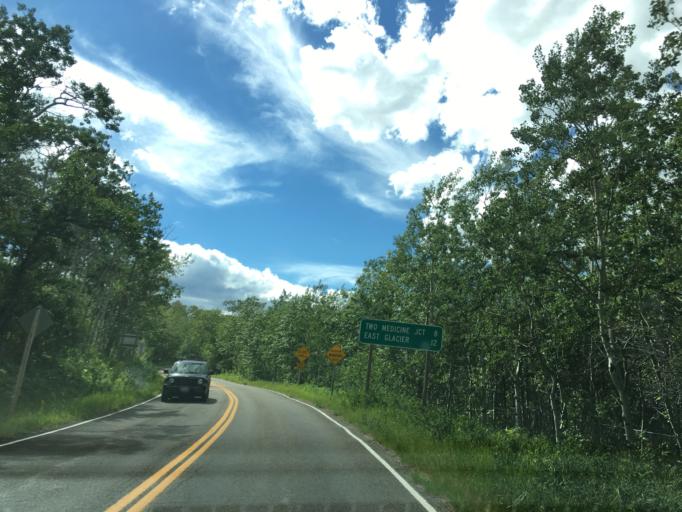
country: US
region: Montana
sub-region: Glacier County
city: South Browning
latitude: 48.5471
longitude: -113.2727
